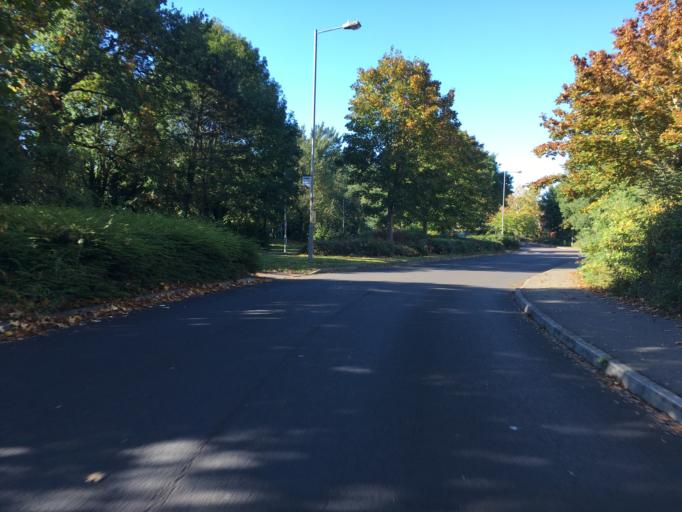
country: GB
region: England
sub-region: Wiltshire
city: Chippenham
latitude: 51.4723
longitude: -2.1357
